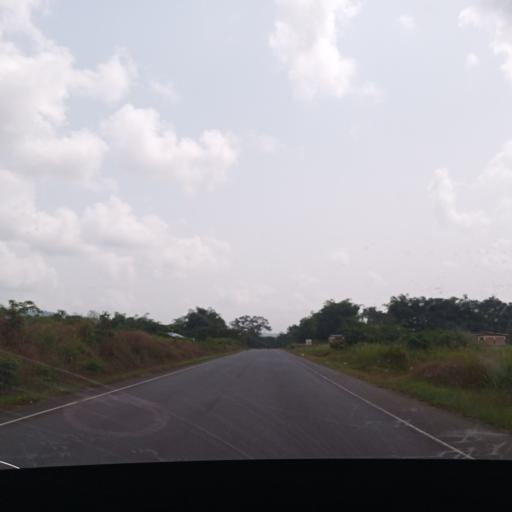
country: LR
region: Margibi
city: Kakata
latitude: 6.2434
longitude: -10.2894
